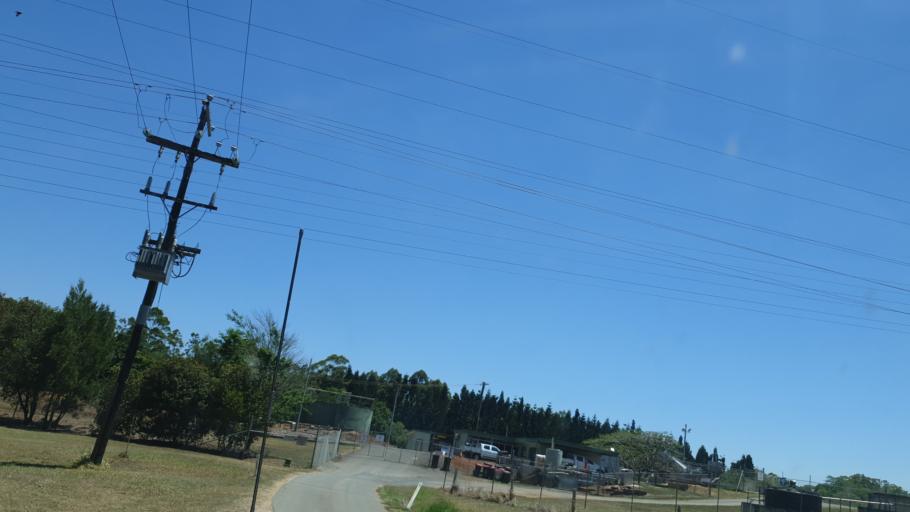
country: AU
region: Queensland
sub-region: Tablelands
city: Atherton
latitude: -17.2551
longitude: 145.4799
